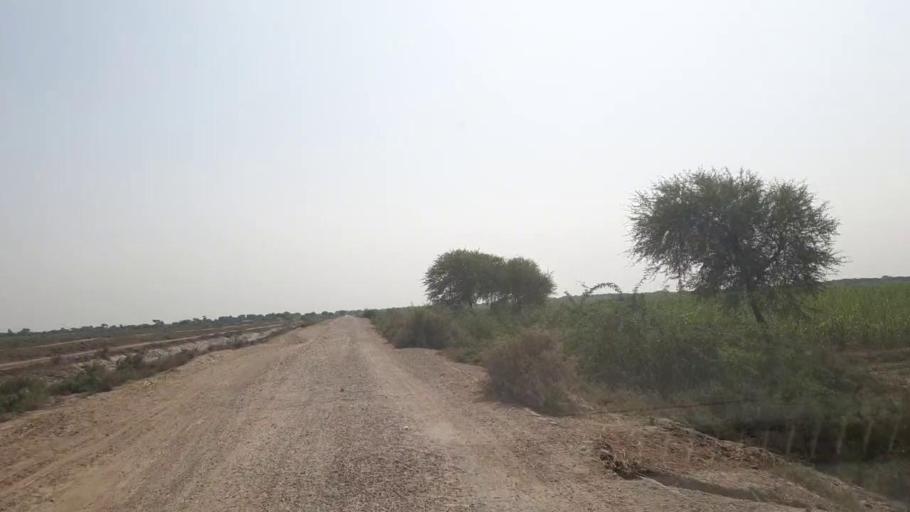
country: PK
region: Sindh
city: Kadhan
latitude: 24.4708
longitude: 68.9038
